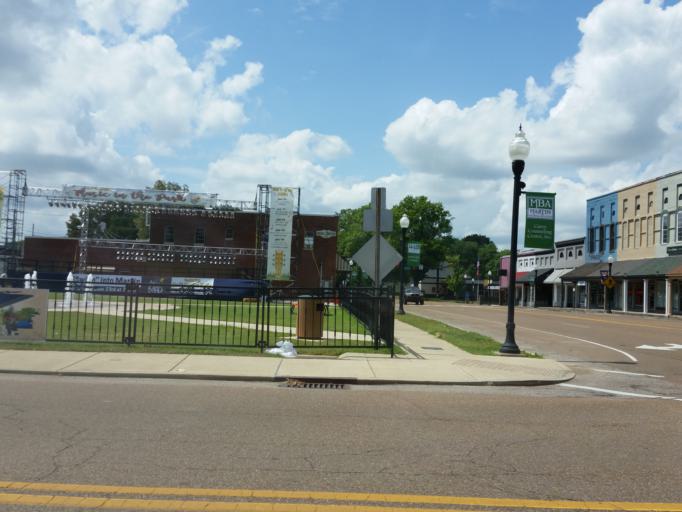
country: US
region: Tennessee
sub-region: Weakley County
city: Martin
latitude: 36.3432
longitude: -88.8503
